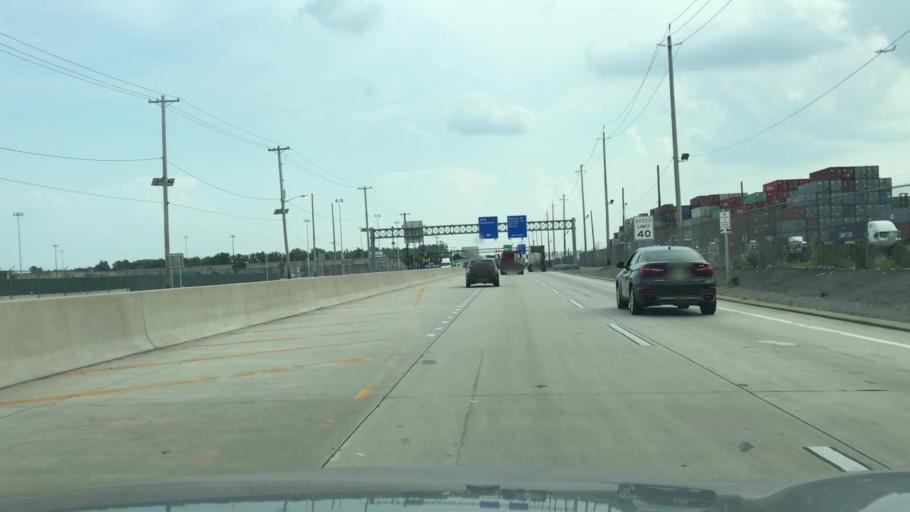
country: US
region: New Jersey
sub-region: Hudson County
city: Bayonne
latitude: 40.6728
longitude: -74.1612
